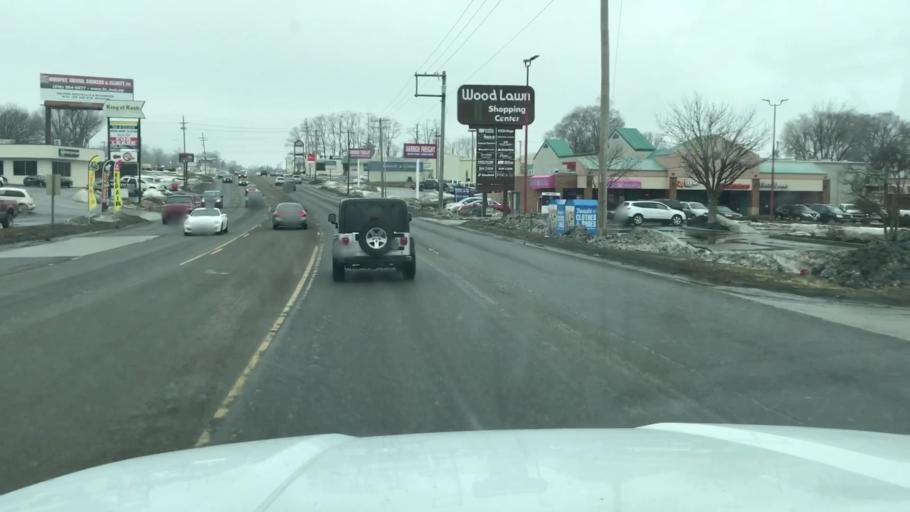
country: US
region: Missouri
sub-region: Buchanan County
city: Saint Joseph
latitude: 39.7865
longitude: -94.8046
